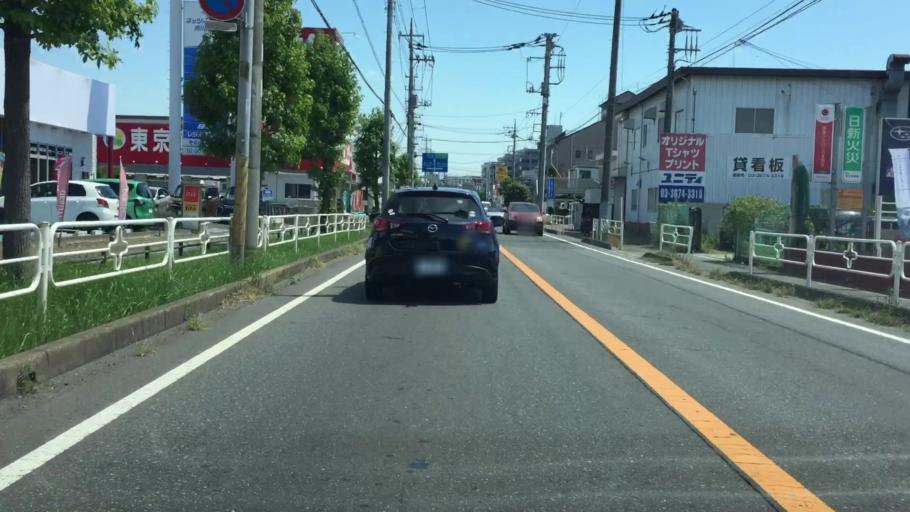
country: JP
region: Chiba
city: Funabashi
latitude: 35.7399
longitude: 139.9503
